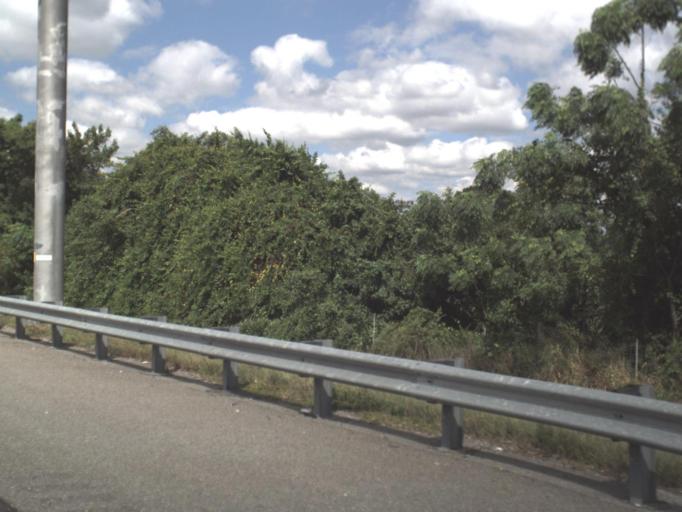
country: US
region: Florida
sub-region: Orange County
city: Gotha
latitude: 28.5295
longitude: -81.5195
